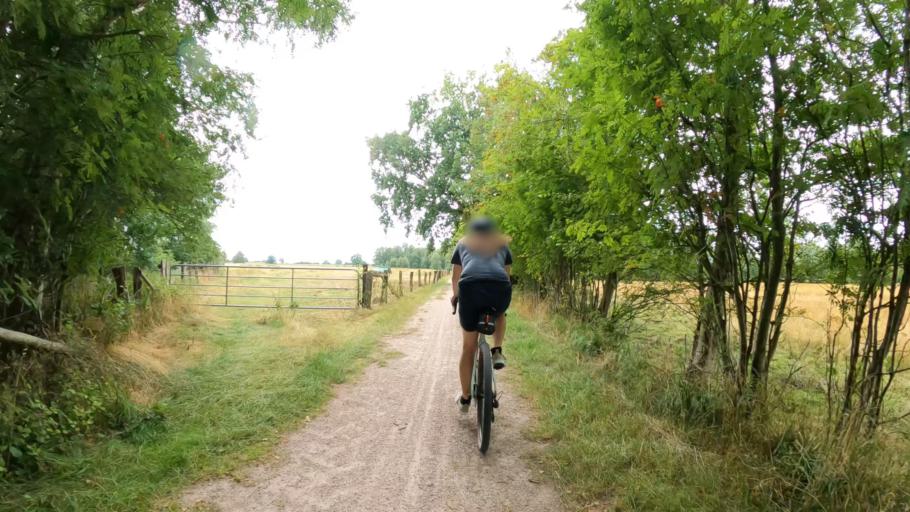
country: DE
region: Schleswig-Holstein
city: Seth
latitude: 53.8532
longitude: 10.2038
